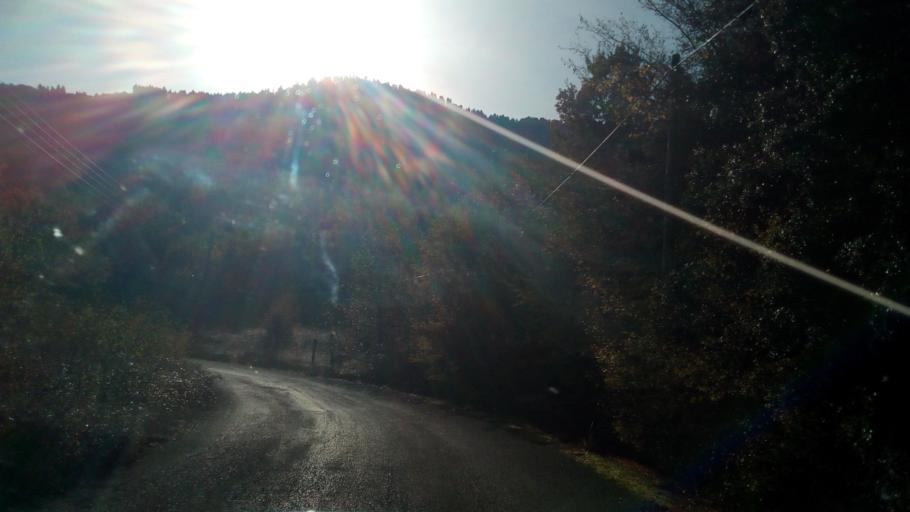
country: GR
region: West Greece
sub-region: Nomos Aitolias kai Akarnanias
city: Thermo
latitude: 38.6547
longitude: 21.8504
